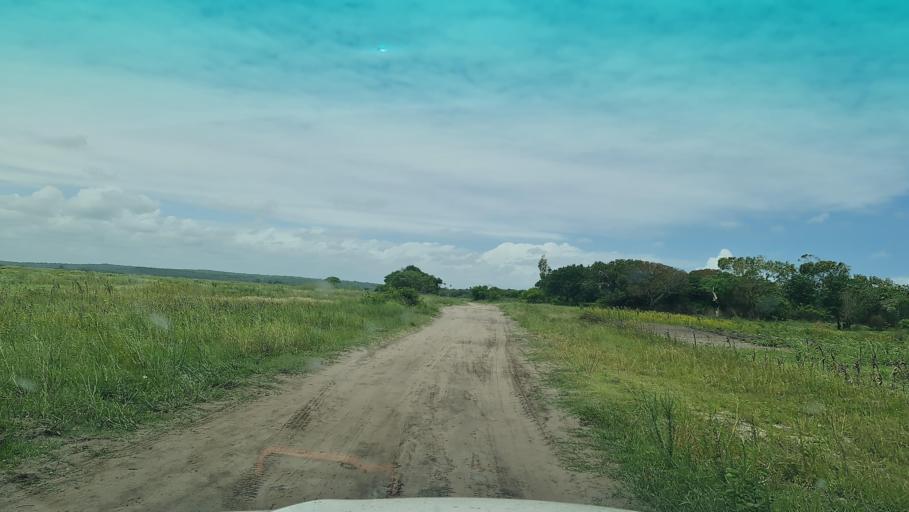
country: MZ
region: Maputo
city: Manhica
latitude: -25.5272
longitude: 32.8529
